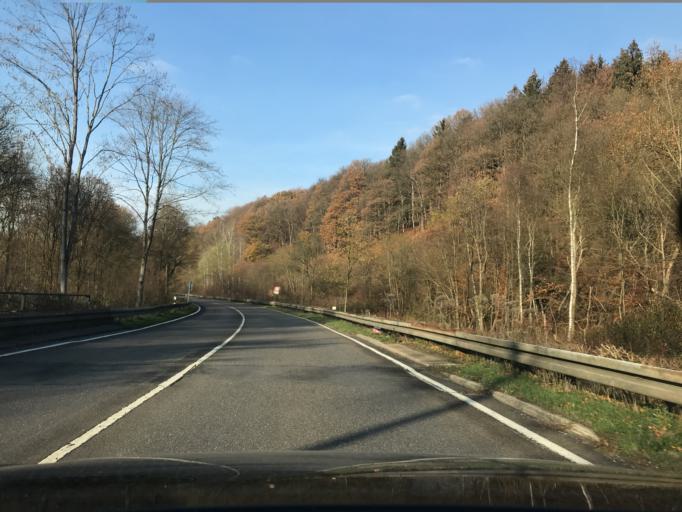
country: DE
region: North Rhine-Westphalia
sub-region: Regierungsbezirk Dusseldorf
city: Solingen
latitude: 51.1832
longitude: 7.1262
